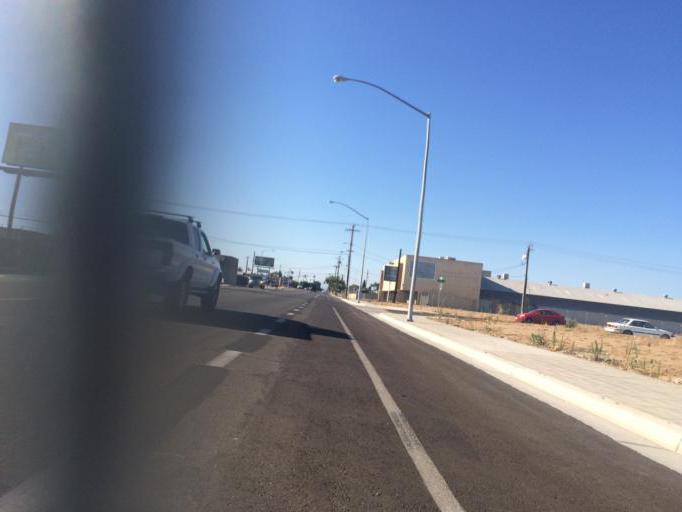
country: US
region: California
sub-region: Fresno County
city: Fresno
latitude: 36.7623
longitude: -119.7454
